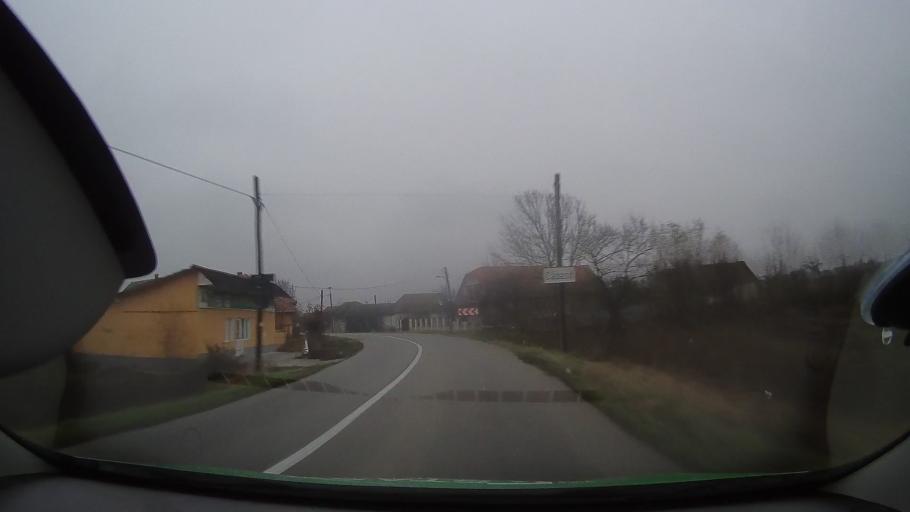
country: RO
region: Bihor
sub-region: Comuna Tulca
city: Tulca
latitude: 46.7868
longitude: 21.8119
